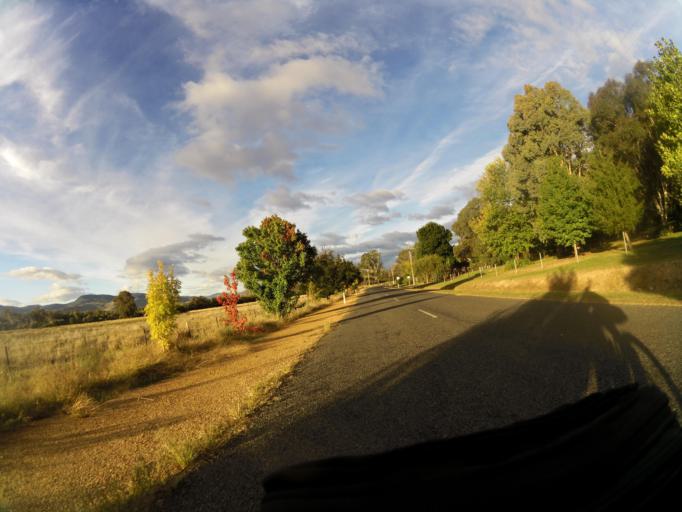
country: AU
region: New South Wales
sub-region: Greater Hume Shire
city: Holbrook
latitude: -36.0468
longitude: 147.9269
